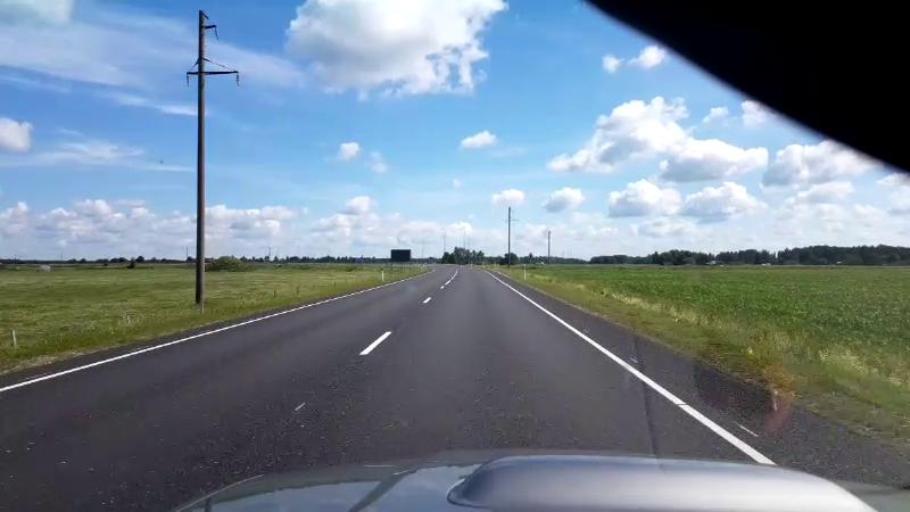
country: EE
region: Jaervamaa
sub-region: Jaerva-Jaani vald
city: Jarva-Jaani
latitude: 59.1383
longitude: 25.7655
